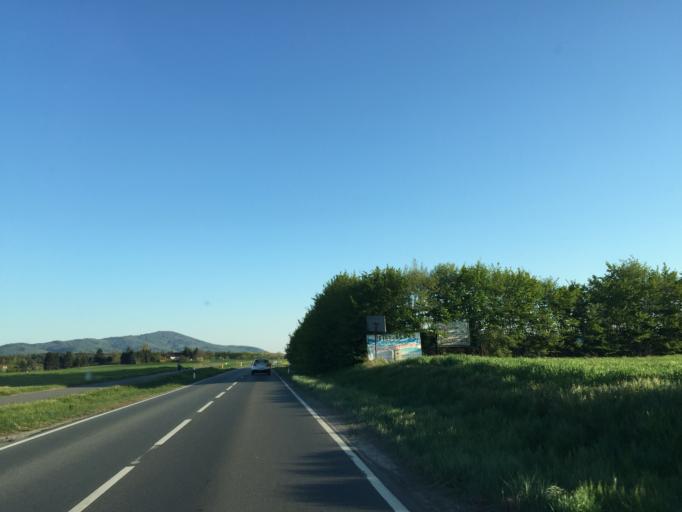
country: DE
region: Hesse
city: Pfungstadt
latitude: 49.7924
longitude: 8.6014
